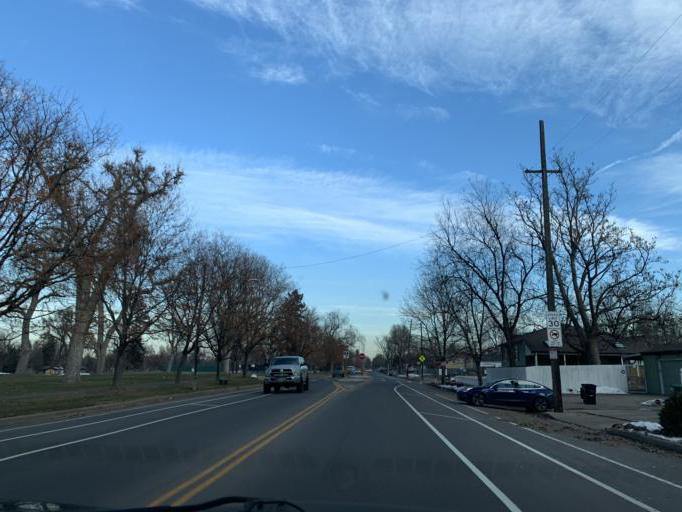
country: US
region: Colorado
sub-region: Jefferson County
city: Edgewater
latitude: 39.7802
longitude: -105.0496
